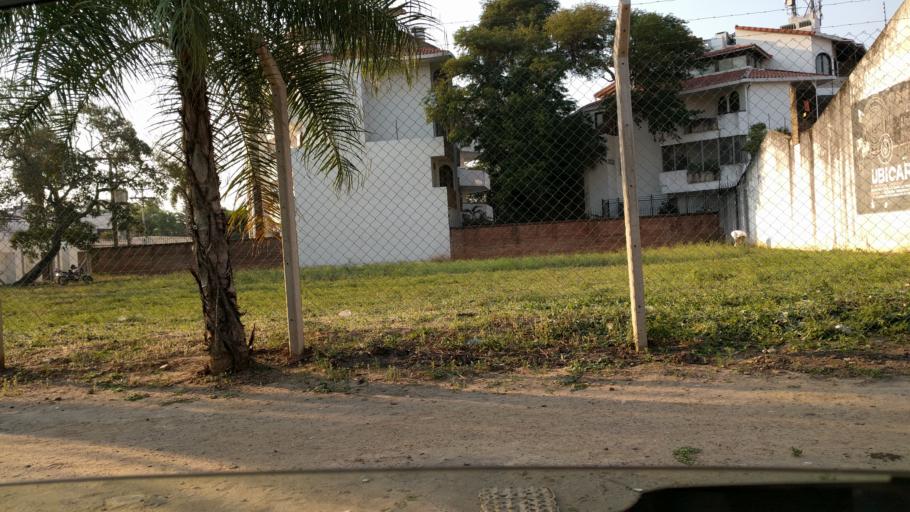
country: BO
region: Santa Cruz
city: Santa Cruz de la Sierra
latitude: -17.8028
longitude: -63.2052
